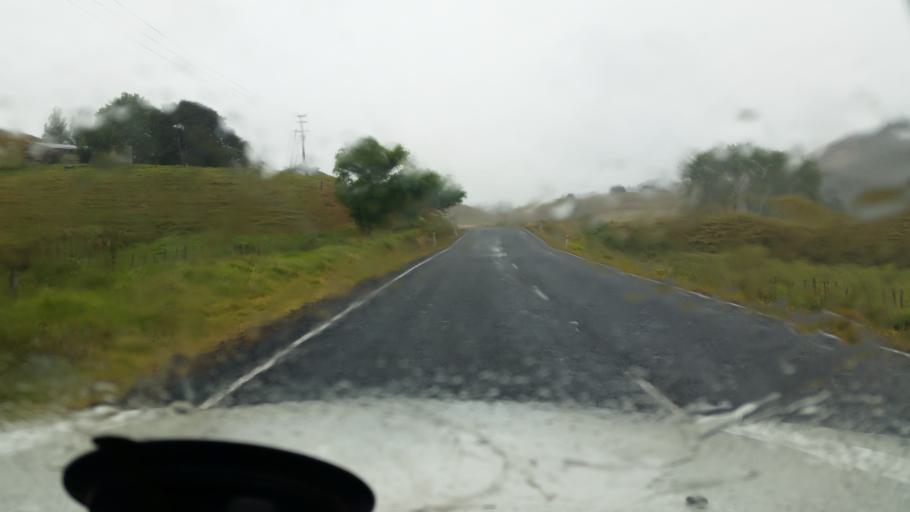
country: NZ
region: Northland
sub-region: Far North District
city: Kaitaia
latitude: -35.2729
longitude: 173.3554
